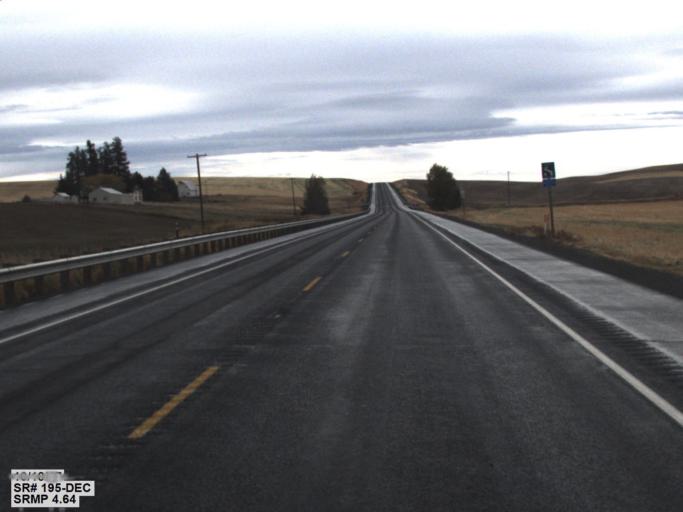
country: US
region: Washington
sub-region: Asotin County
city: Clarkston
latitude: 46.5313
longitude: -117.0853
